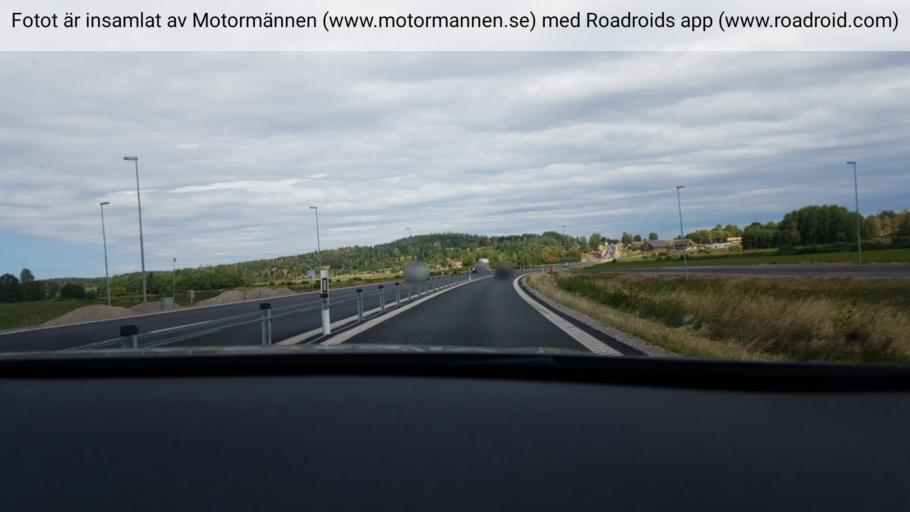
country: SE
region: Joenkoeping
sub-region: Tranas Kommun
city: Tranas
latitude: 58.0021
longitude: 14.9207
